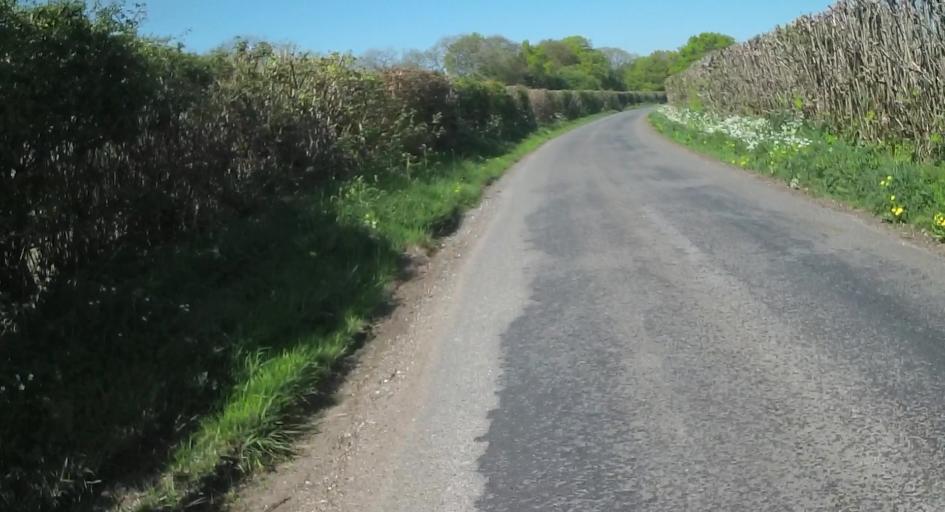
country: GB
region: England
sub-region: Hampshire
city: Four Marks
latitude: 51.1353
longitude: -1.0409
